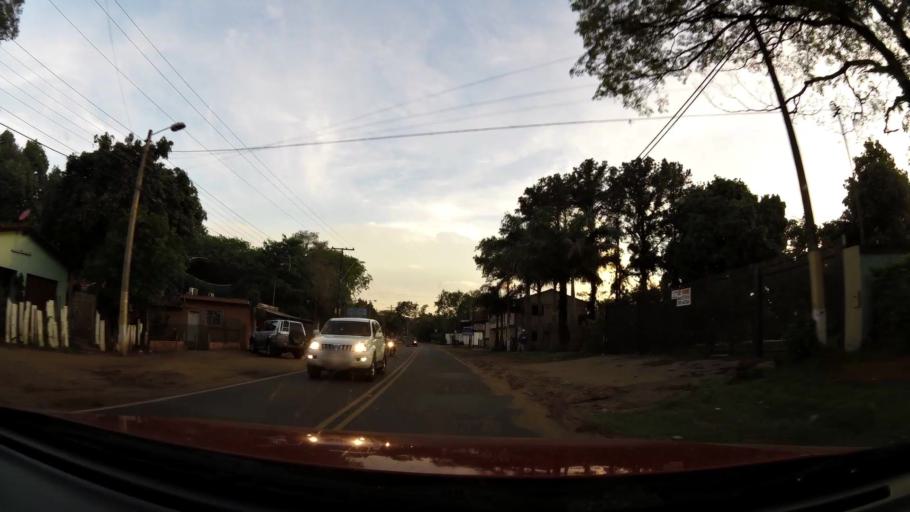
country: PY
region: Central
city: San Lorenzo
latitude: -25.3580
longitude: -57.4910
